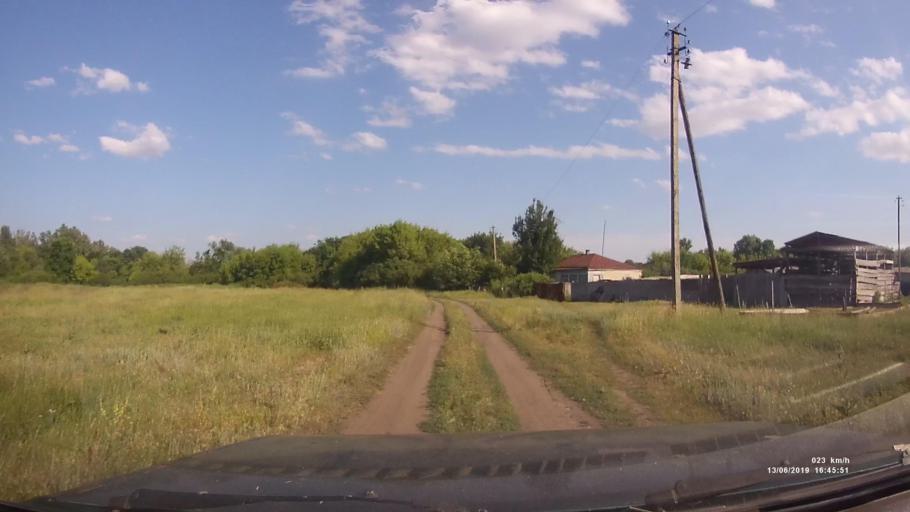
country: RU
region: Rostov
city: Kazanskaya
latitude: 49.9467
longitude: 41.4247
